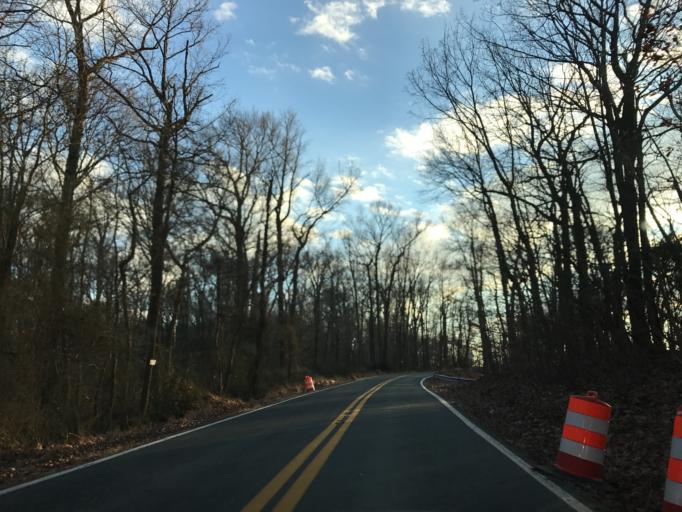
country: US
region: Maryland
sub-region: Cecil County
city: Charlestown
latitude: 39.4746
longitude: -75.9925
